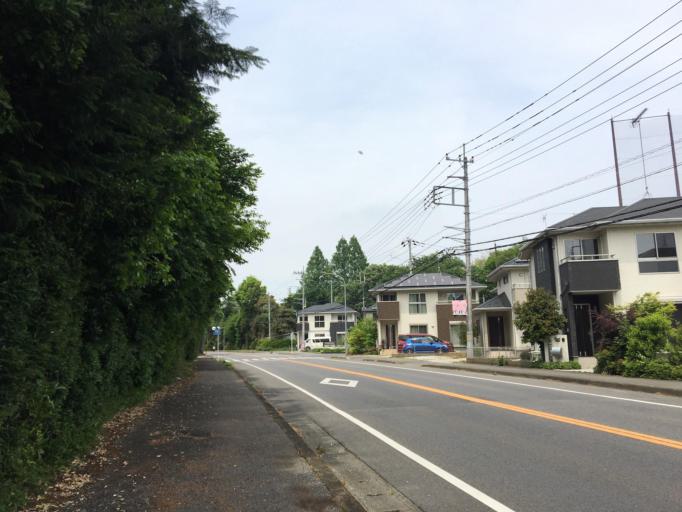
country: JP
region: Tochigi
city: Oyama
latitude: 36.3412
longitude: 139.8165
